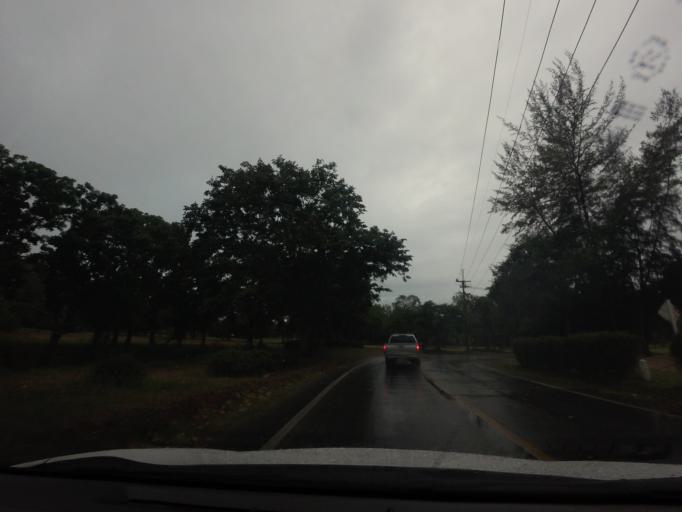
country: TH
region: Chon Buri
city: Sattahip
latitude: 12.7016
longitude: 100.9571
